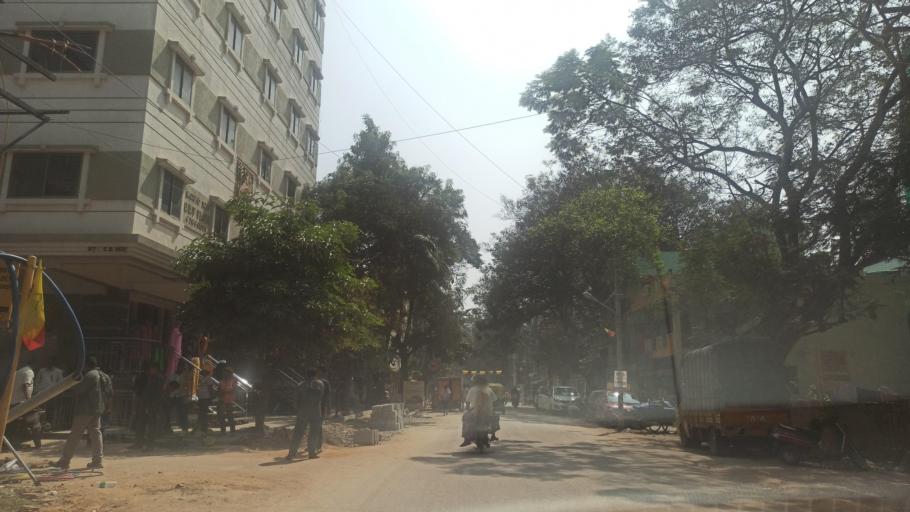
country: IN
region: Karnataka
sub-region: Bangalore Urban
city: Bangalore
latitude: 12.9638
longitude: 77.7131
